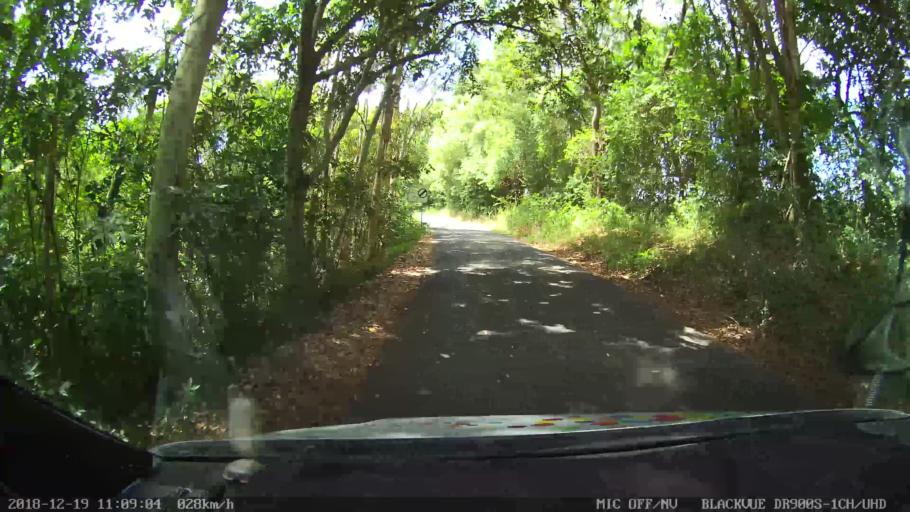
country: AU
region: New South Wales
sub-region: Lismore Municipality
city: Nimbin
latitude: -28.6326
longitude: 153.2640
